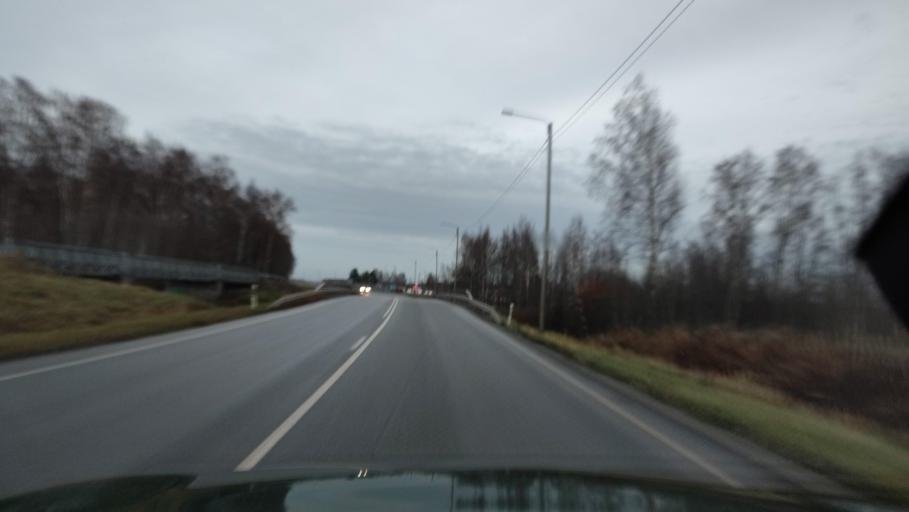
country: FI
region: Ostrobothnia
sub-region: Vaasa
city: Ristinummi
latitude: 63.0408
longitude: 21.7405
